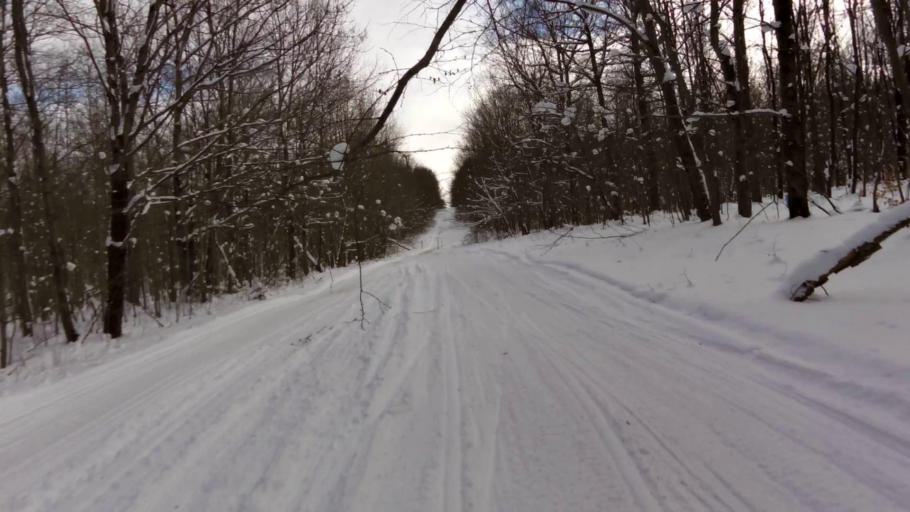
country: US
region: New York
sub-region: Cattaraugus County
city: Franklinville
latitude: 42.3089
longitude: -78.5308
